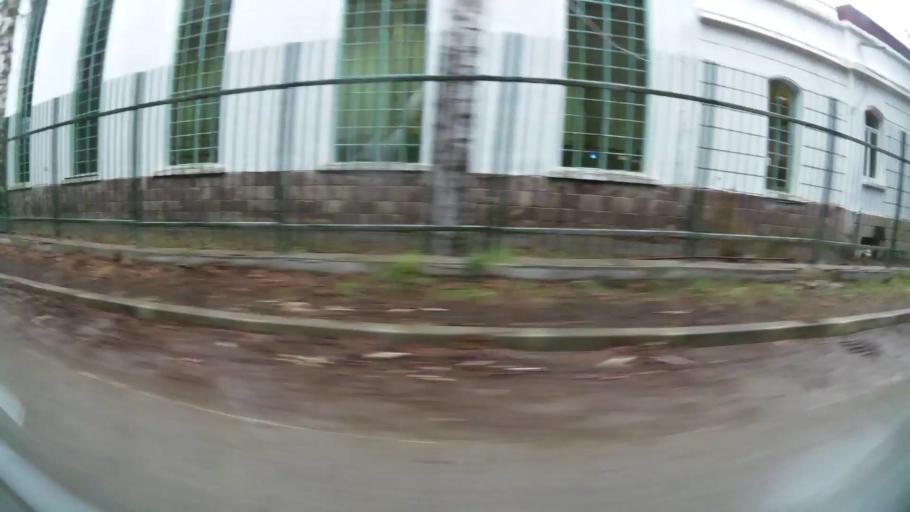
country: BG
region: Sofia-Capital
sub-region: Stolichna Obshtina
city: Sofia
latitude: 42.5841
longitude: 23.4284
